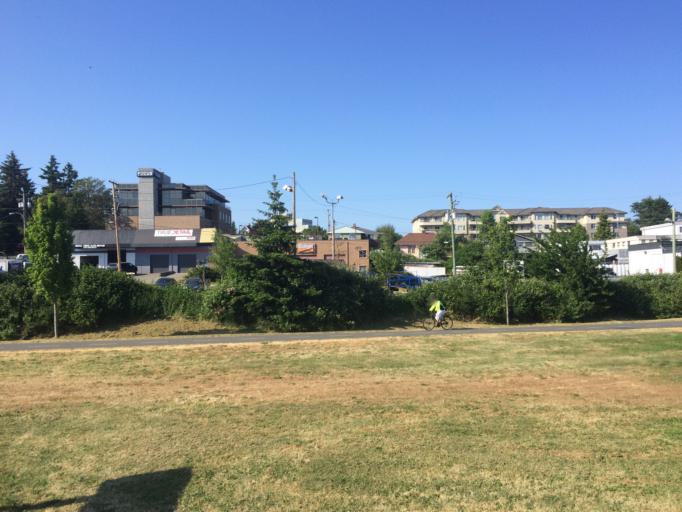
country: CA
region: British Columbia
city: Victoria
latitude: 48.4558
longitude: -123.3800
